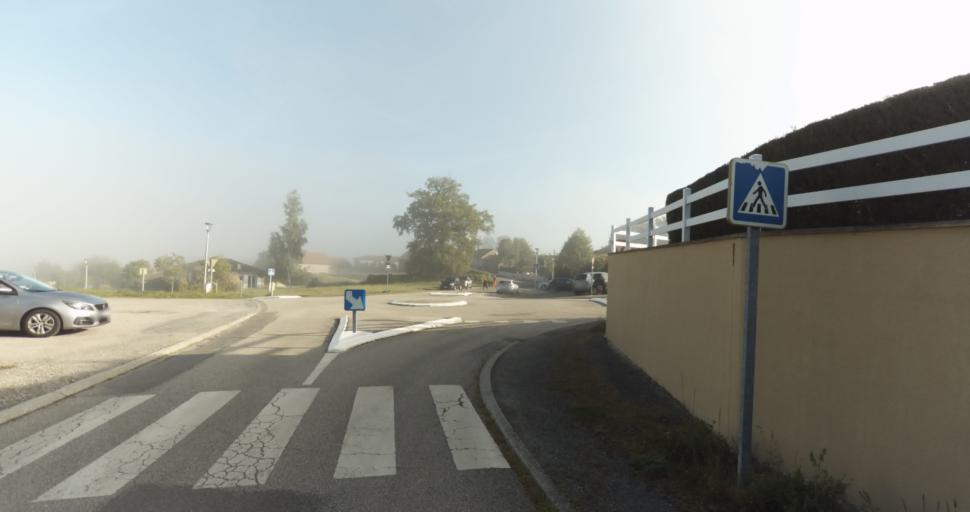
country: FR
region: Limousin
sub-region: Departement de la Haute-Vienne
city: Condat-sur-Vienne
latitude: 45.7832
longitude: 1.2834
